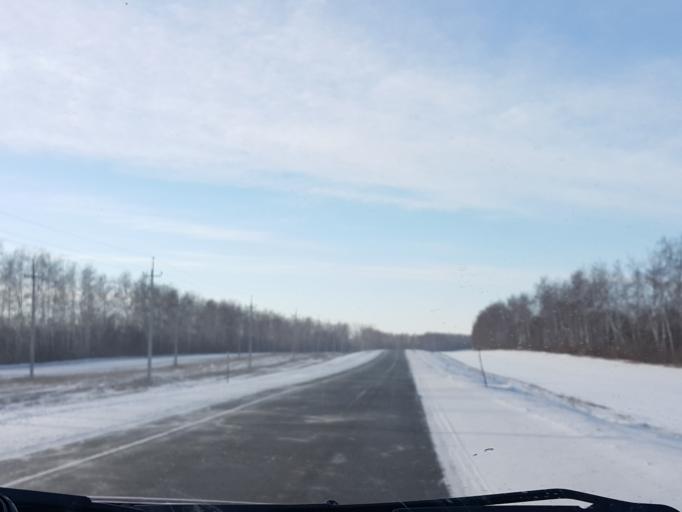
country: RU
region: Tambov
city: Znamenka
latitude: 52.3850
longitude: 41.3368
